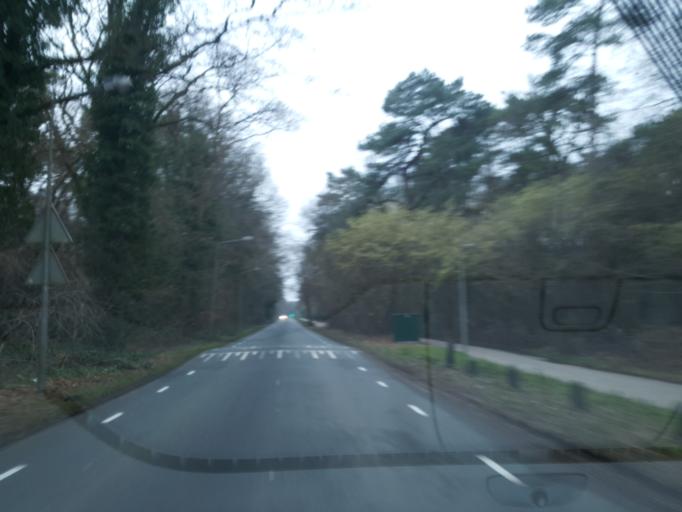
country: NL
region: North Holland
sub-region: Gemeente Wijdemeren
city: Nieuw-Loosdrecht
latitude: 52.1904
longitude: 5.1639
